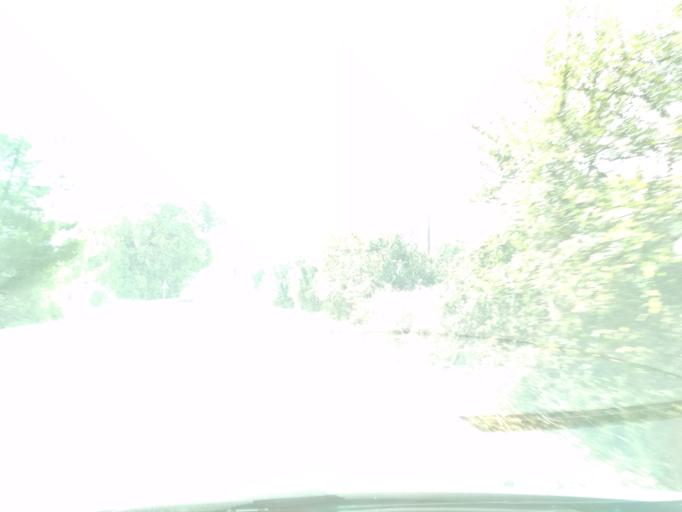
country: GR
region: Central Greece
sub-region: Nomos Evvoias
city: Prokopion
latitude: 38.7261
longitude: 23.5043
